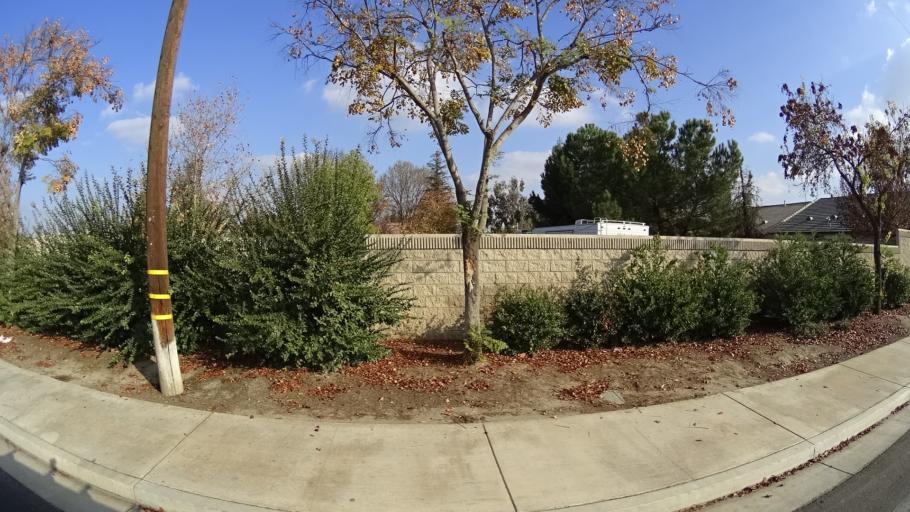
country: US
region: California
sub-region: Kern County
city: Greenacres
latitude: 35.3052
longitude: -119.1098
